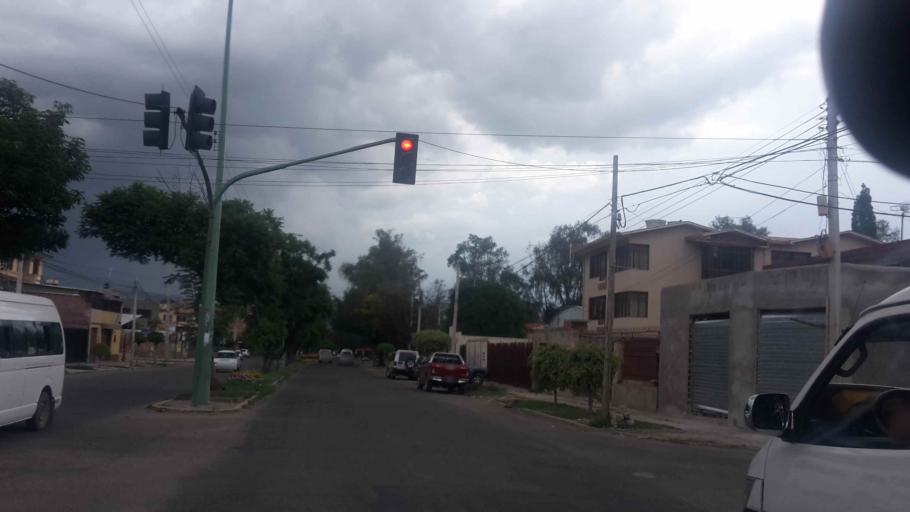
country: BO
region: Cochabamba
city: Cochabamba
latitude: -17.3928
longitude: -66.1410
